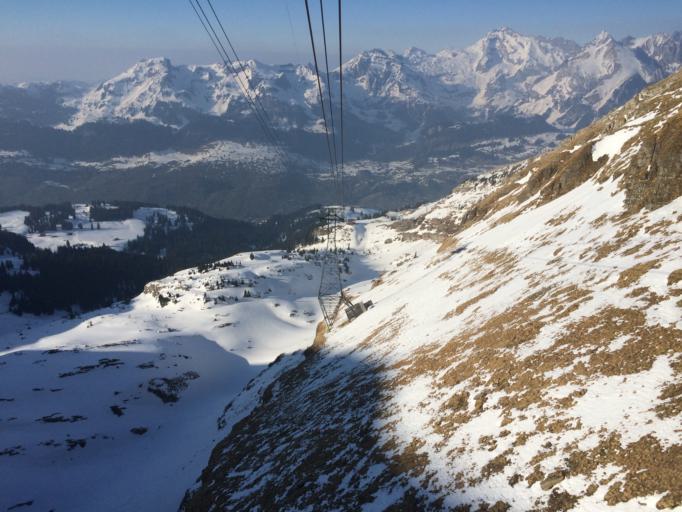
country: CH
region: Saint Gallen
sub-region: Wahlkreis Sarganserland
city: Walenstadt
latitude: 47.1599
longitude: 9.3123
